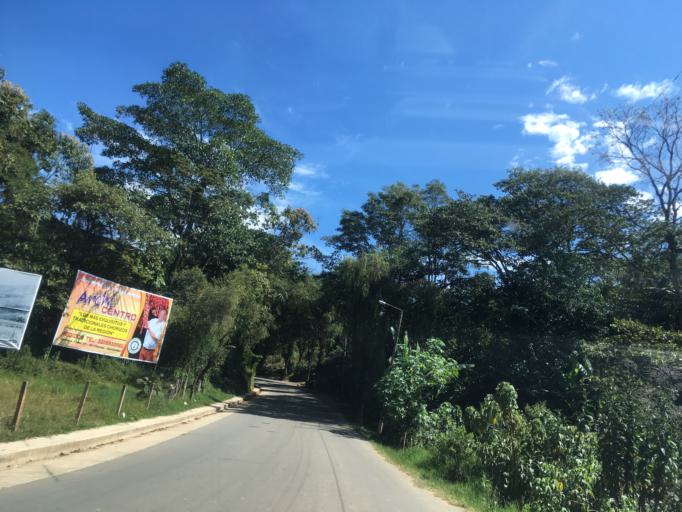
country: CO
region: Santander
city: Coromoro
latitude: 6.2853
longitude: -73.1529
